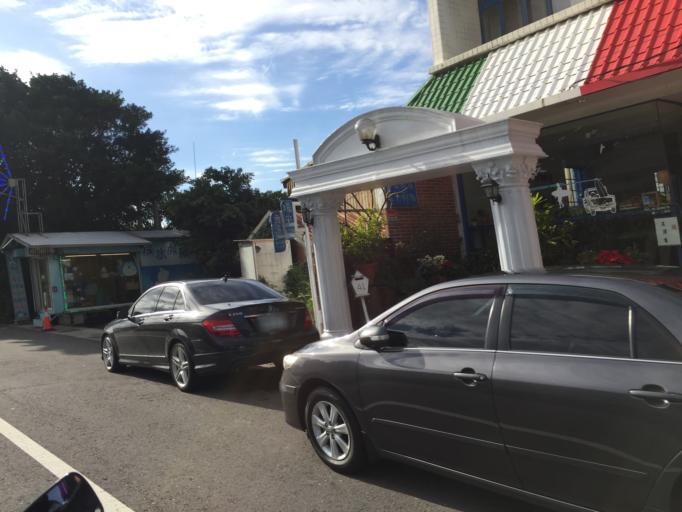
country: TW
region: Taipei
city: Taipei
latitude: 25.2527
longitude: 121.4721
